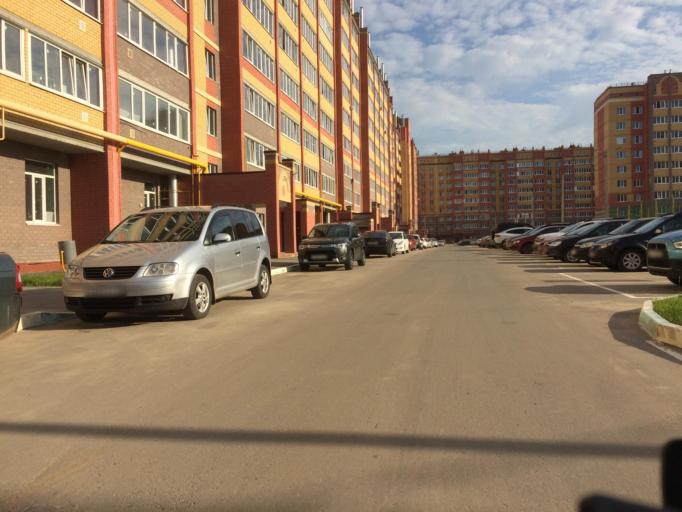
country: RU
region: Mariy-El
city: Medvedevo
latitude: 56.6371
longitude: 47.8200
